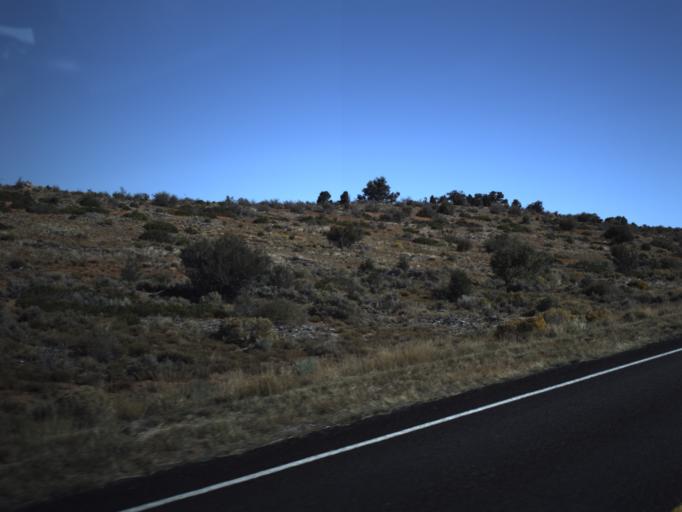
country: US
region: Utah
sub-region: Iron County
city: Cedar City
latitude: 37.6112
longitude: -113.3481
